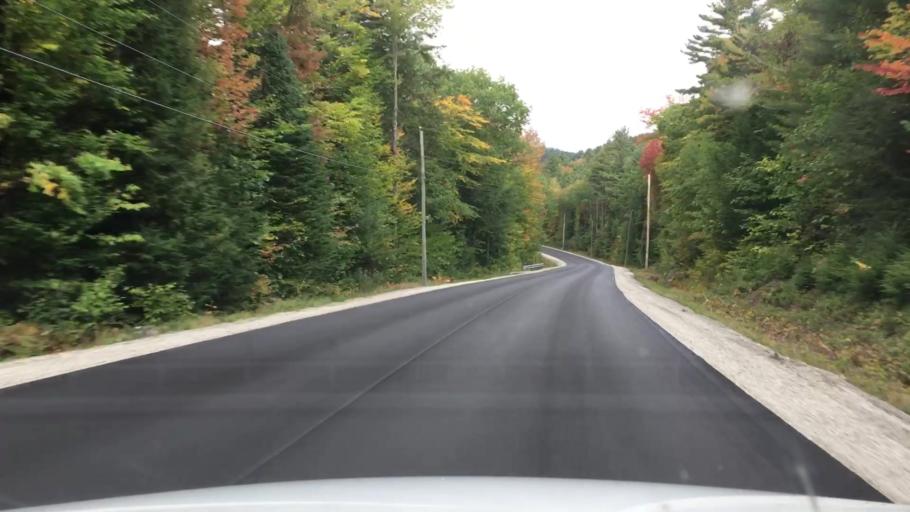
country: US
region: Maine
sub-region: Oxford County
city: Bethel
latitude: 44.3121
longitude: -70.7577
